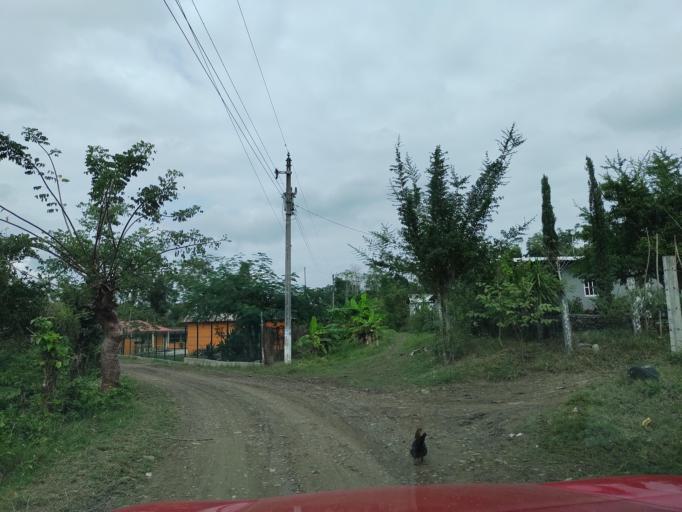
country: MX
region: Veracruz
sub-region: Coatzintla
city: Manuel Maria Contreras
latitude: 20.4440
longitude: -97.4419
